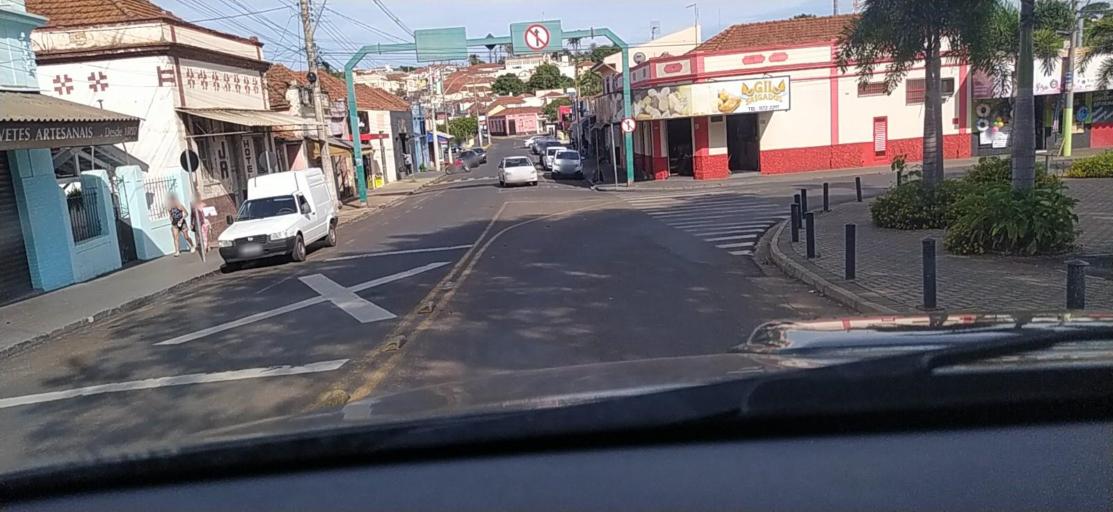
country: BR
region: Sao Paulo
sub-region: Pindorama
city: Pindorama
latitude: -21.1887
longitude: -48.9041
